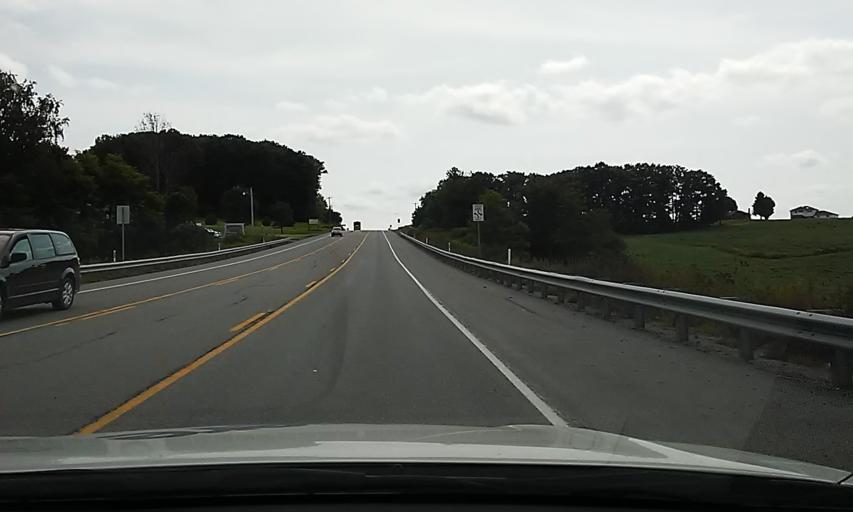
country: US
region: Pennsylvania
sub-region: Jefferson County
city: Punxsutawney
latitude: 40.9232
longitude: -78.9852
